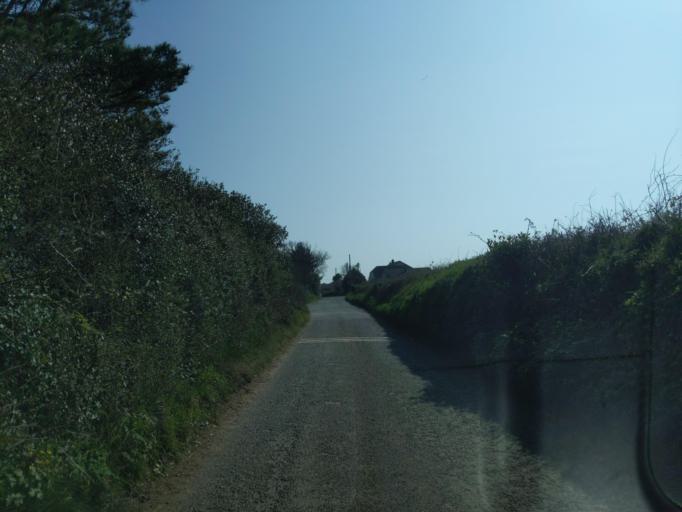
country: GB
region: England
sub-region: Devon
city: Dartmouth
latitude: 50.3148
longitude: -3.6325
